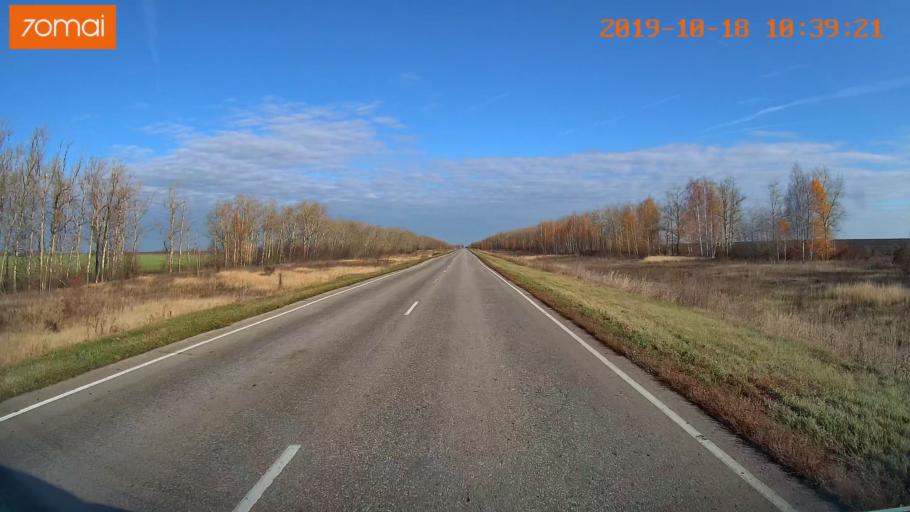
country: RU
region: Tula
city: Kurkino
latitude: 53.5857
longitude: 38.6519
